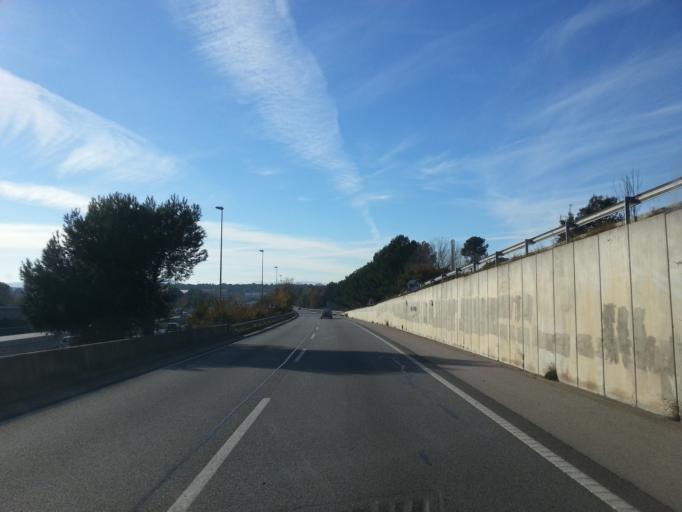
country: ES
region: Catalonia
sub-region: Provincia de Barcelona
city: Sant Cugat del Valles
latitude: 41.4919
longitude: 2.0944
